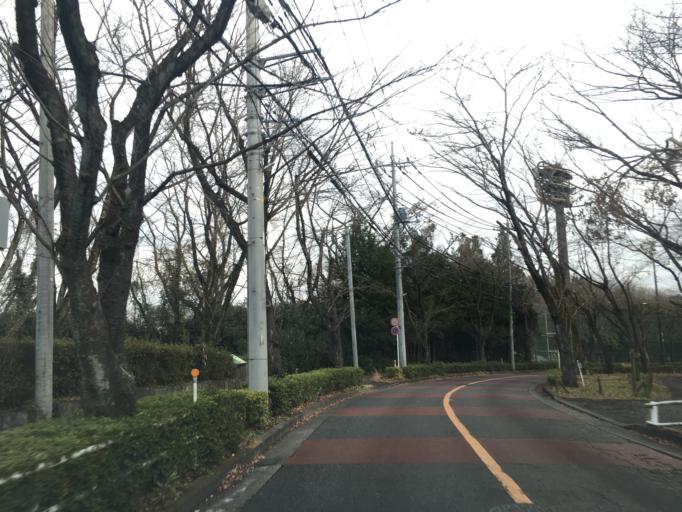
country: JP
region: Tokyo
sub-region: Machida-shi
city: Machida
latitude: 35.6075
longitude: 139.4312
